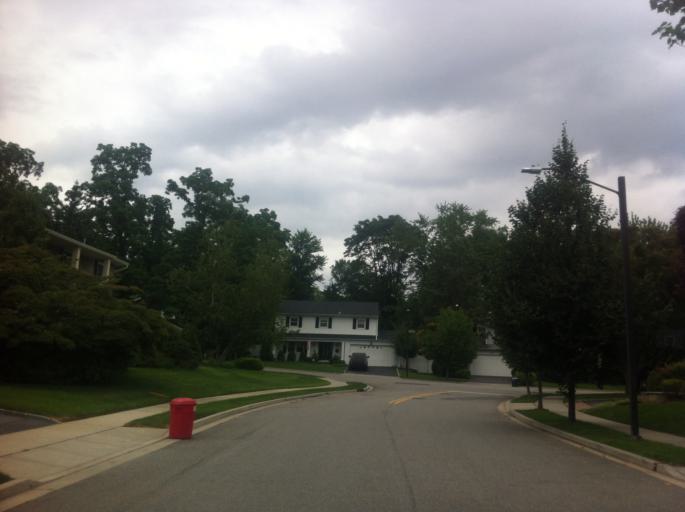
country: US
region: New York
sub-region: Nassau County
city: Lattingtown
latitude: 40.9046
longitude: -73.5839
